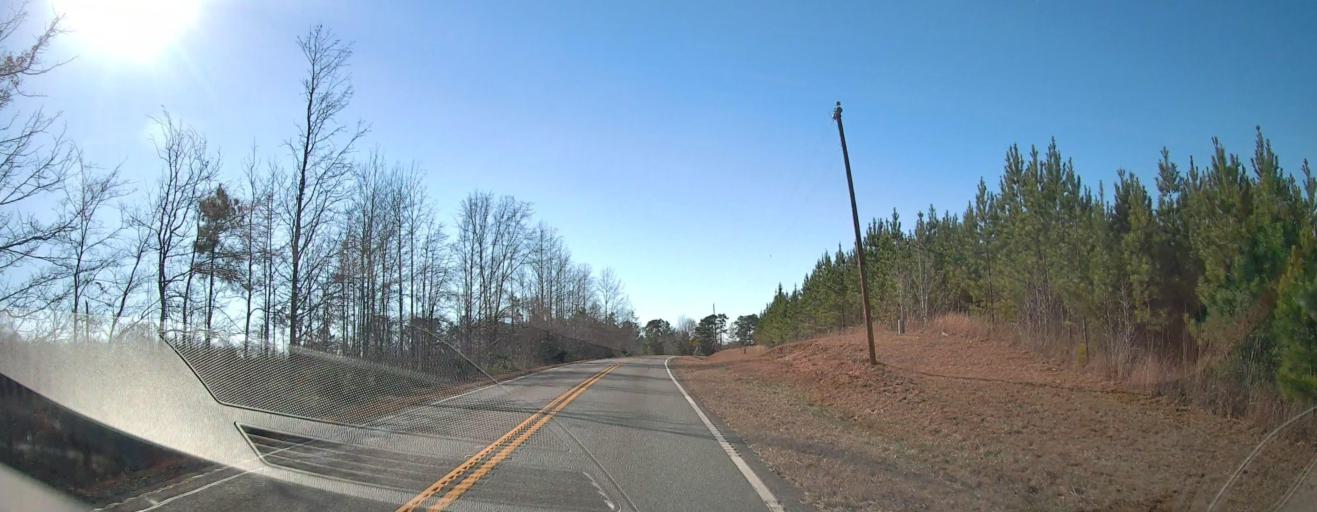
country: US
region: Georgia
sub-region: Talbot County
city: Talbotton
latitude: 32.6510
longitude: -84.4514
